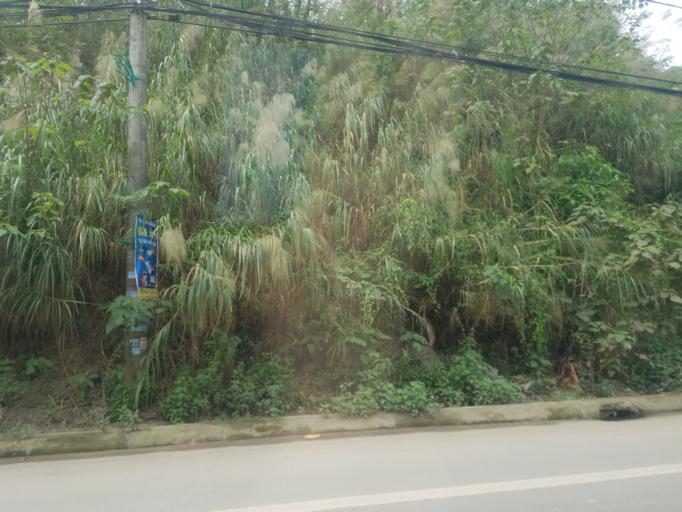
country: VN
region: Thai Nguyen
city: Chua Hang
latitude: 21.6120
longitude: 105.8399
